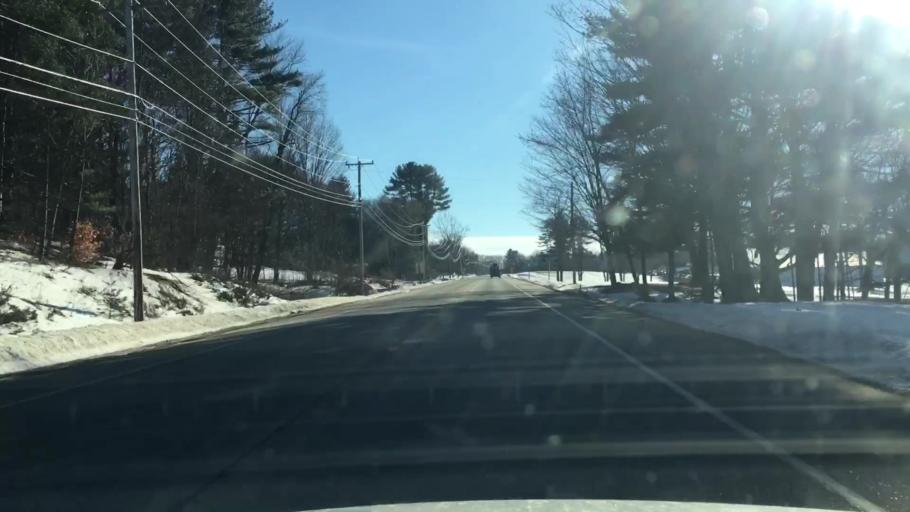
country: US
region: Maine
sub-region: Cumberland County
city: North Windham
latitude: 43.8076
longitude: -70.4038
